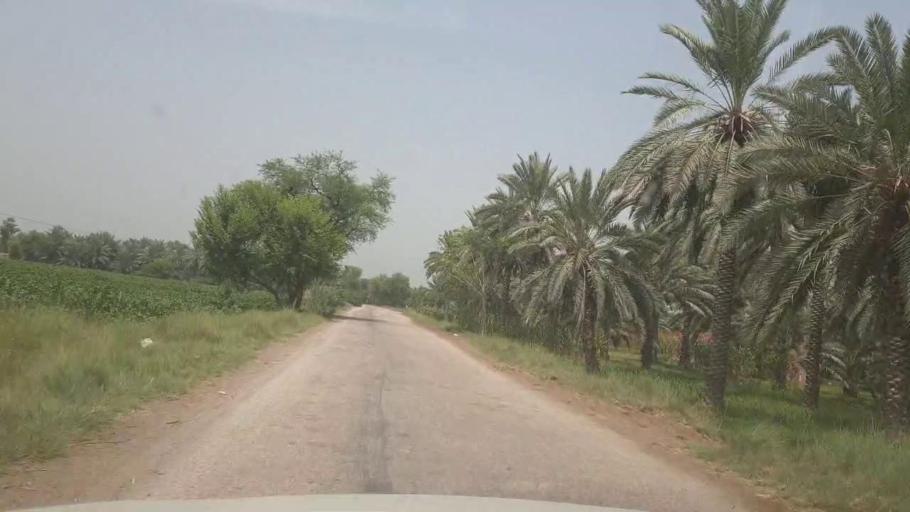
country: PK
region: Sindh
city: Kot Diji
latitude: 27.3651
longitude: 68.6529
